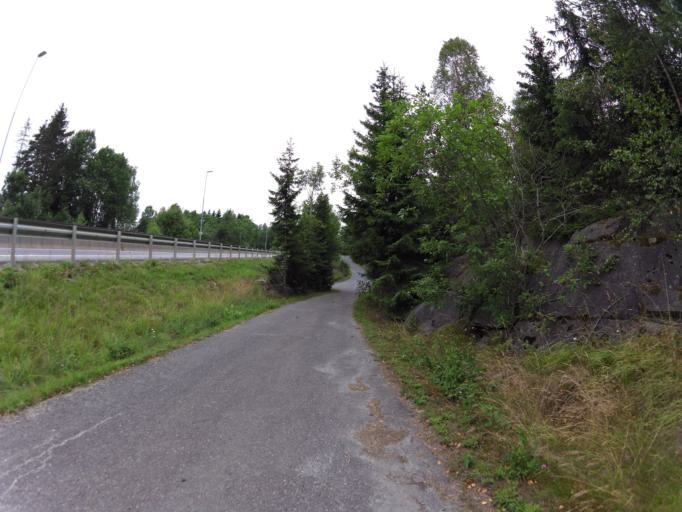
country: NO
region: Akershus
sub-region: Vestby
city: Vestby
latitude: 59.5669
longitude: 10.7368
